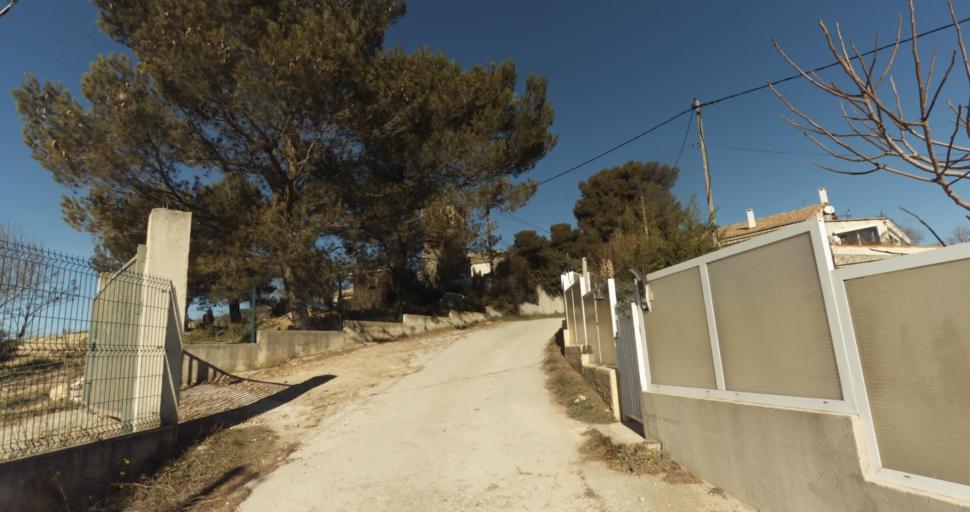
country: FR
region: Provence-Alpes-Cote d'Azur
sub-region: Departement des Bouches-du-Rhone
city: Cadolive
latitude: 43.3833
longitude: 5.5581
